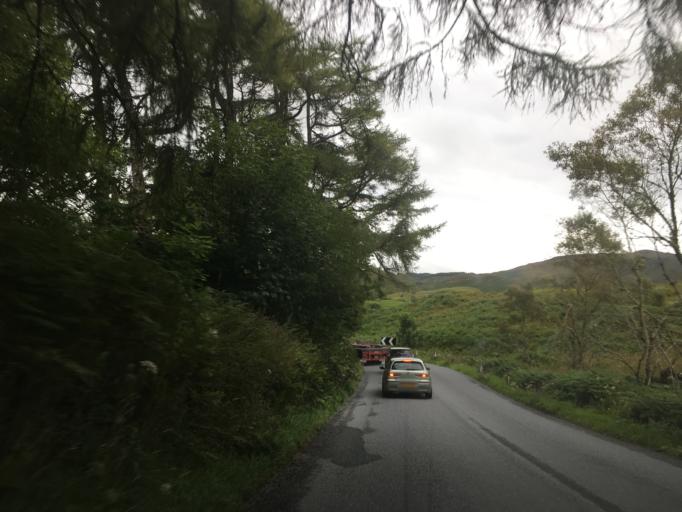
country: GB
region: Scotland
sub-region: Argyll and Bute
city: Oban
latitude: 56.2652
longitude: -5.4785
